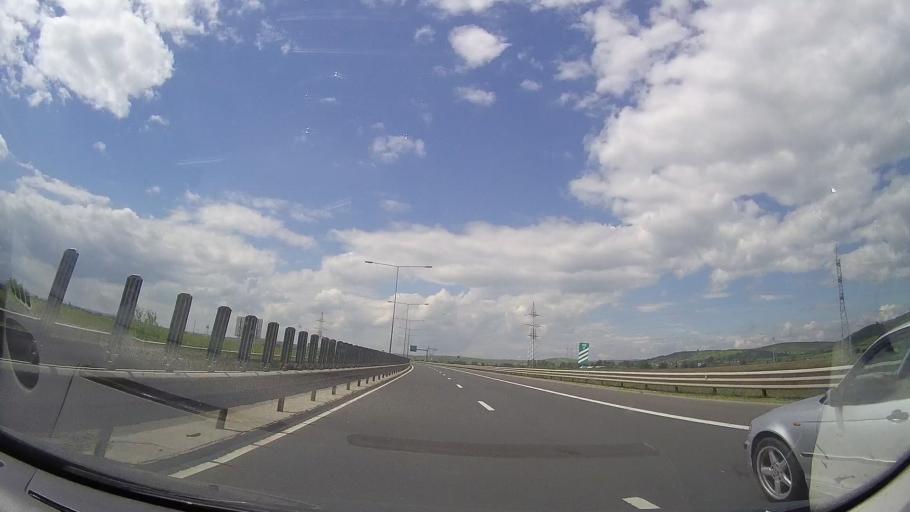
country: RO
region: Sibiu
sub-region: Municipiul Sibiu
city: Sibiu
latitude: 45.8172
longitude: 24.1643
